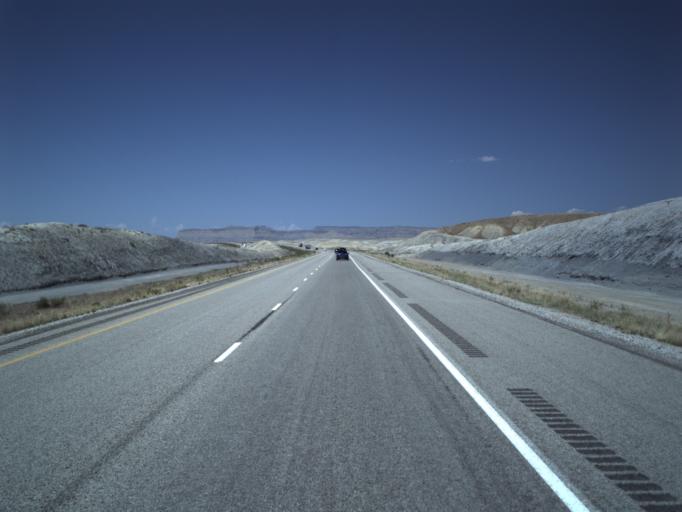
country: US
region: Utah
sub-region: Grand County
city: Moab
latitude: 38.9404
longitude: -110.0329
